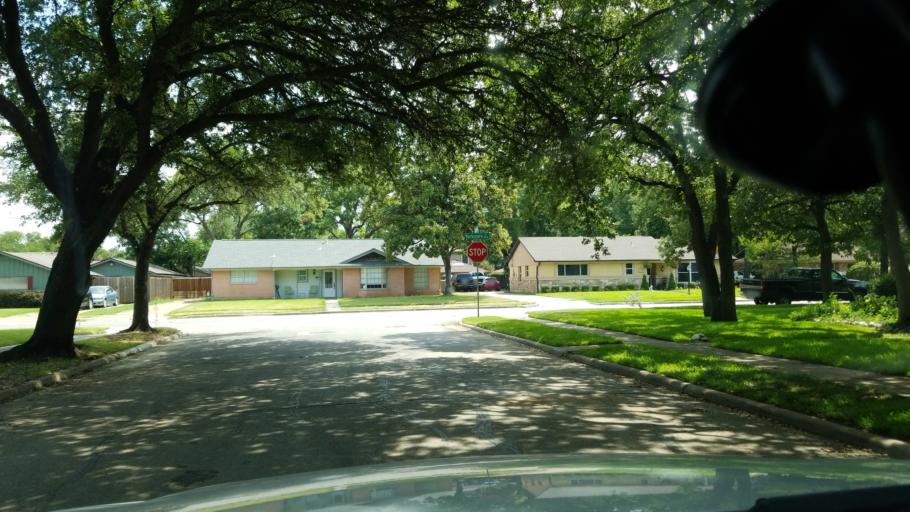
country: US
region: Texas
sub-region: Dallas County
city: Irving
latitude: 32.8188
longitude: -96.9838
